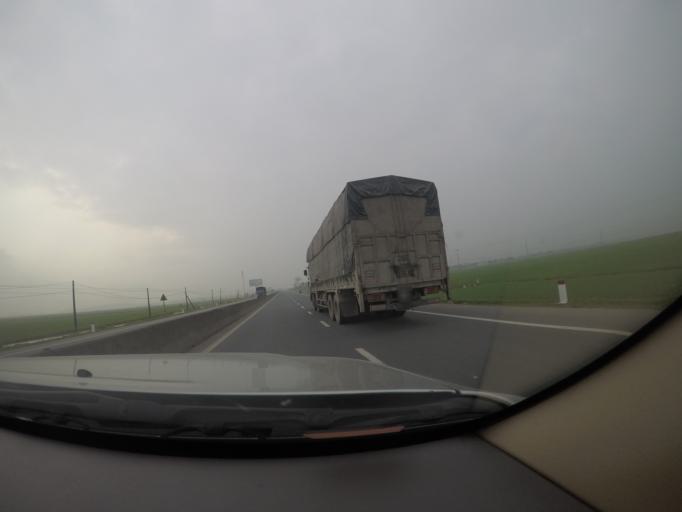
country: VN
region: Ha Tinh
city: Ky Anh
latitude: 18.1812
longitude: 106.2035
